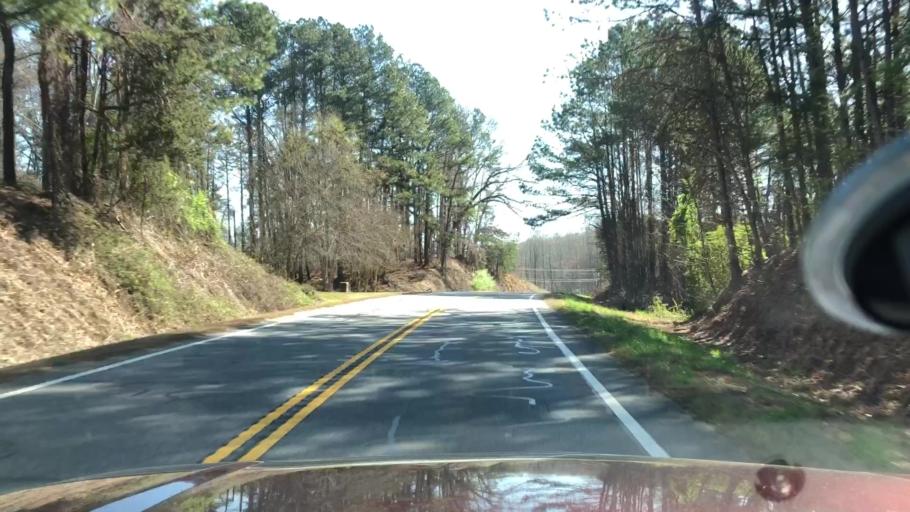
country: US
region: Georgia
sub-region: Cherokee County
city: Canton
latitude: 34.2822
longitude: -84.5660
